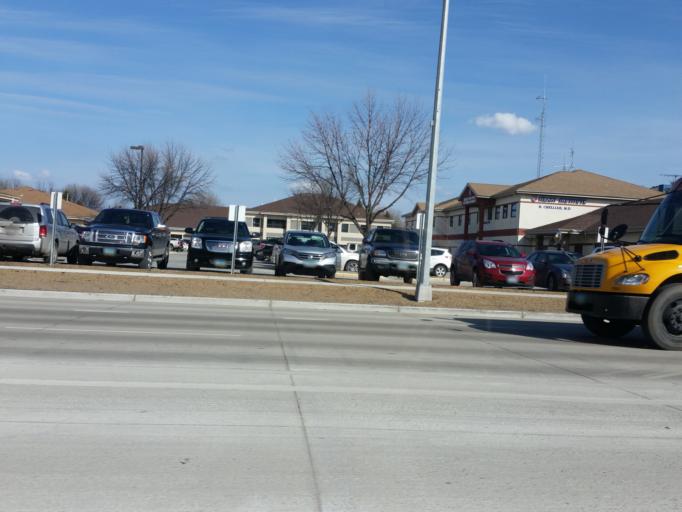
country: US
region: North Dakota
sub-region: Grand Forks County
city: Grand Forks
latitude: 47.9107
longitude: -97.0662
